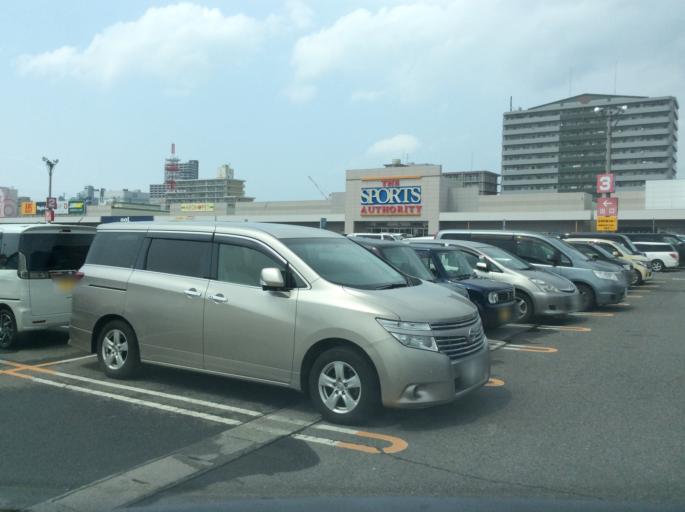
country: JP
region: Fukushima
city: Koriyama
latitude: 37.3899
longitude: 140.3900
